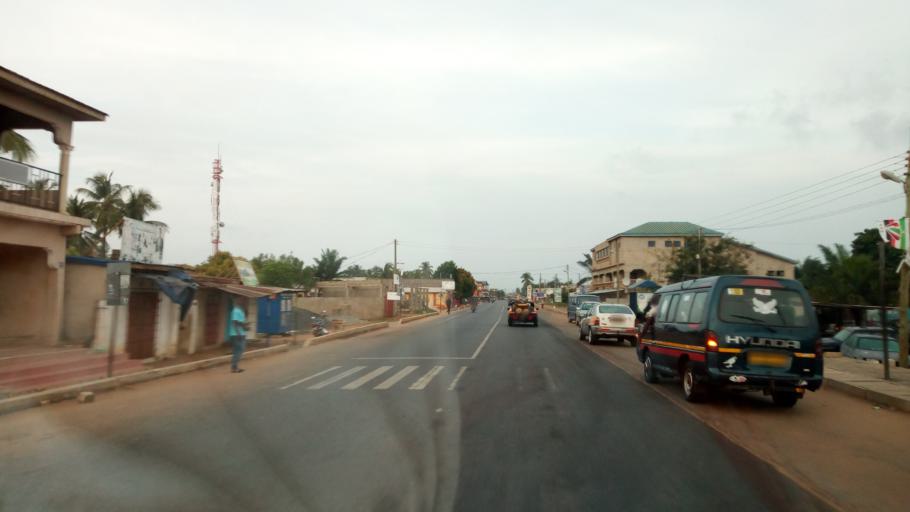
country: TG
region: Maritime
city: Lome
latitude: 6.1198
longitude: 1.1798
